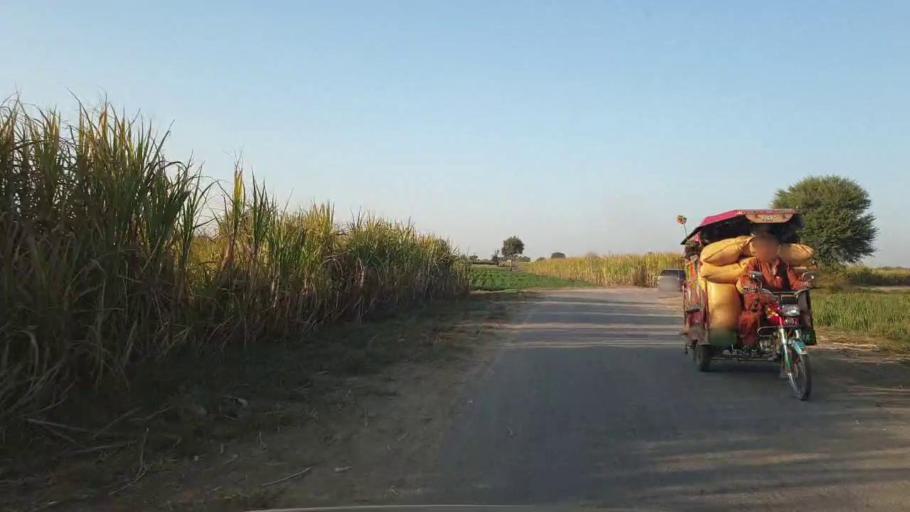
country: PK
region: Sindh
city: Chambar
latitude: 25.3617
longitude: 68.7400
